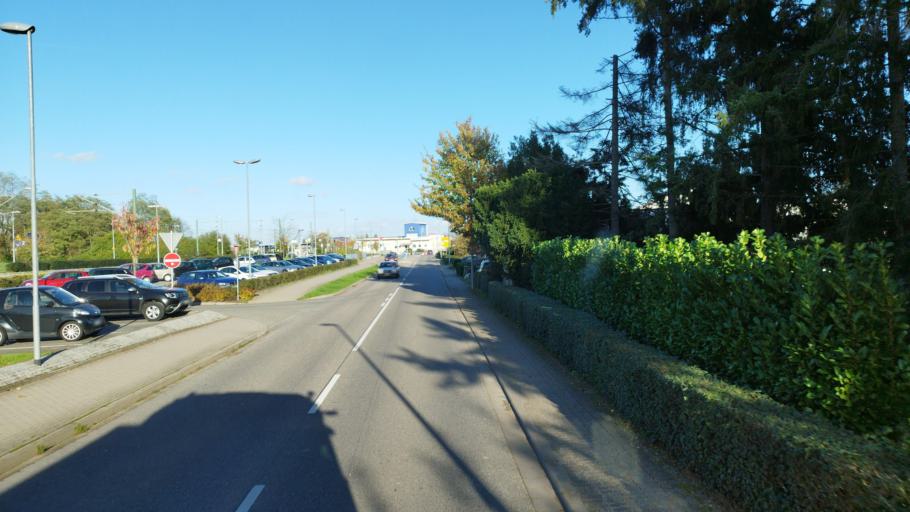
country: DE
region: Rheinland-Pfalz
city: Rulzheim
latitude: 49.1600
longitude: 8.2891
